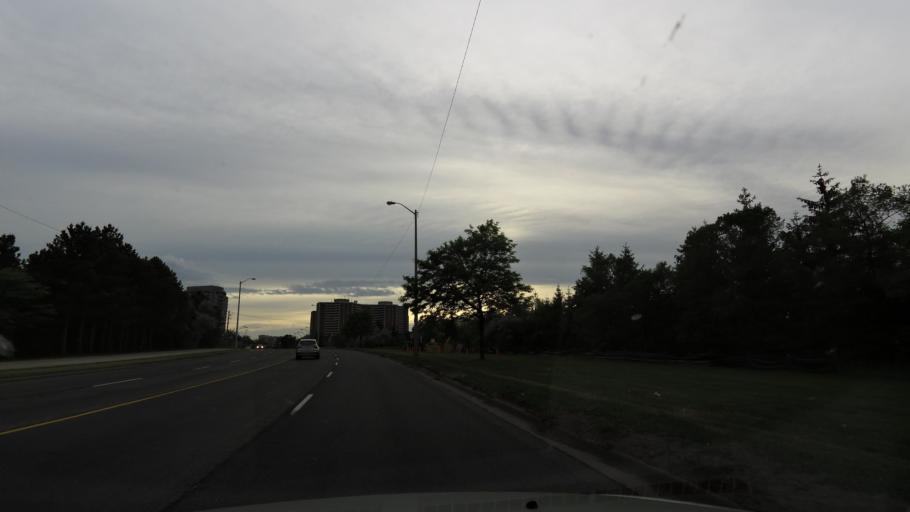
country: CA
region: Ontario
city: Etobicoke
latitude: 43.6847
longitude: -79.5062
